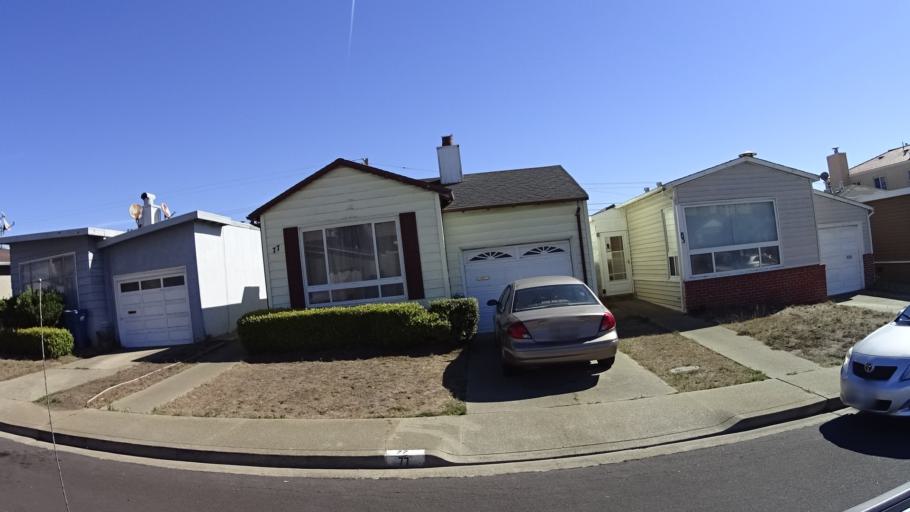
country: US
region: California
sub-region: San Mateo County
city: Broadmoor
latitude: 37.6795
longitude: -122.4860
